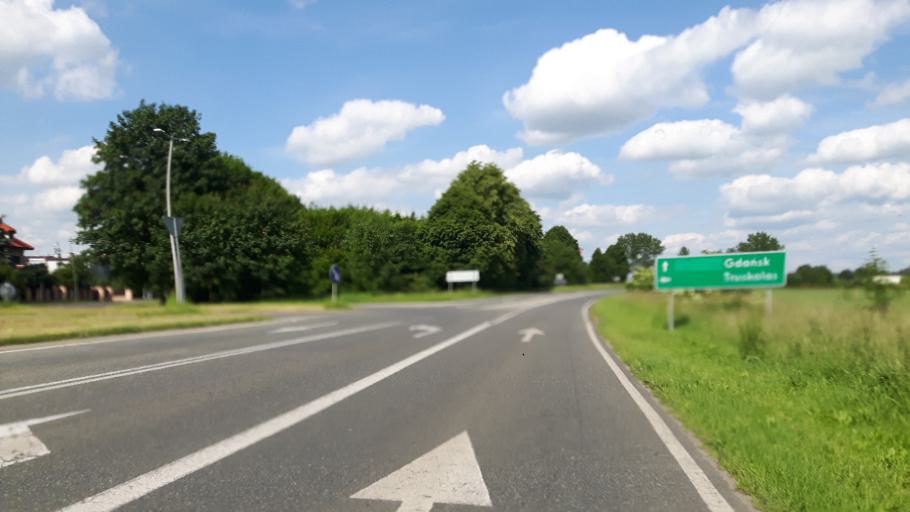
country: PL
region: West Pomeranian Voivodeship
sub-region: Powiat goleniowski
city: Nowogard
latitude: 53.6815
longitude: 15.1191
